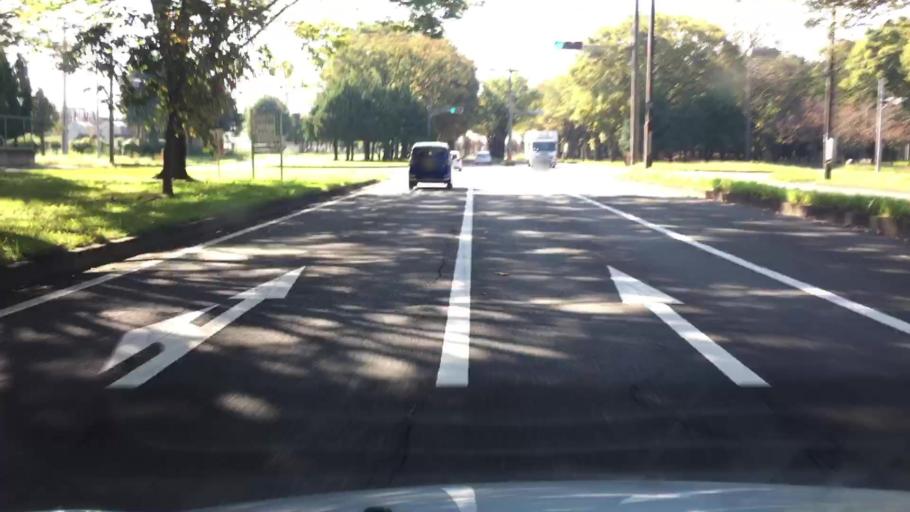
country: JP
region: Tochigi
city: Utsunomiya-shi
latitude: 36.5390
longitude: 139.9876
